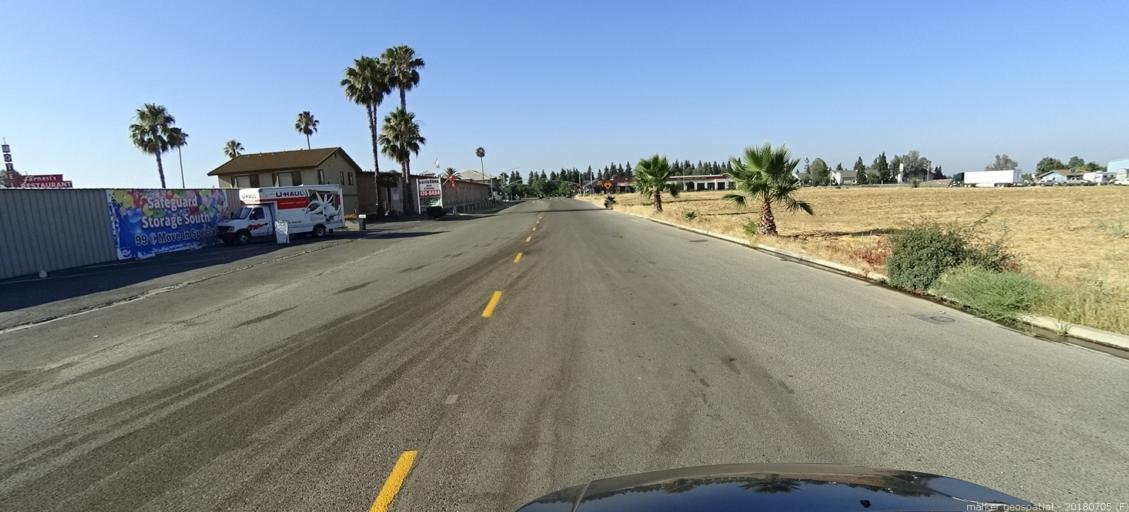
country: US
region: California
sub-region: Madera County
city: Madera
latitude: 36.9836
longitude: -120.0877
